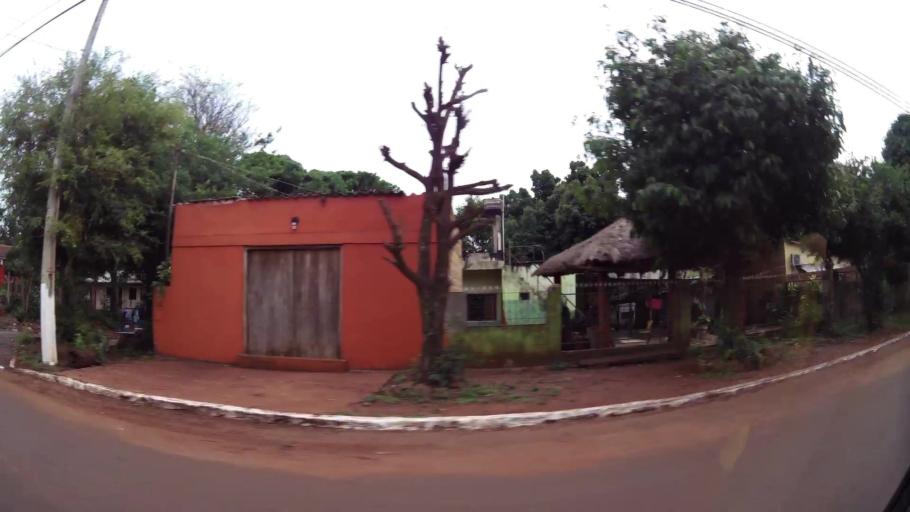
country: BR
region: Parana
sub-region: Foz Do Iguacu
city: Foz do Iguacu
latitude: -25.5635
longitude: -54.6050
